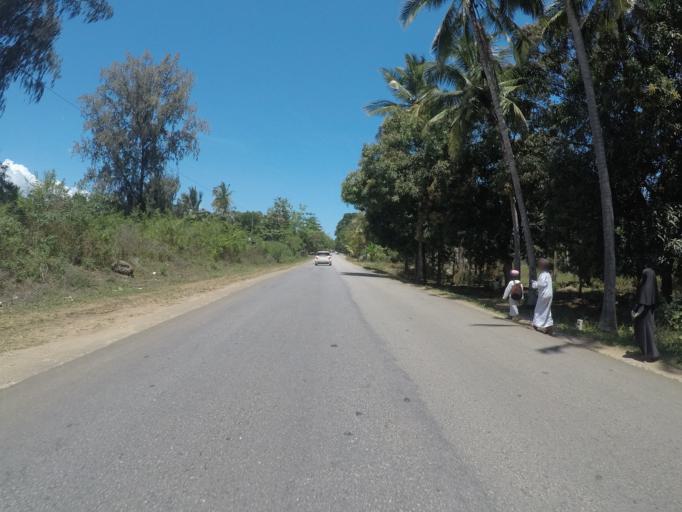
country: TZ
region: Zanzibar Central/South
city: Koani
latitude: -6.2408
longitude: 39.3284
